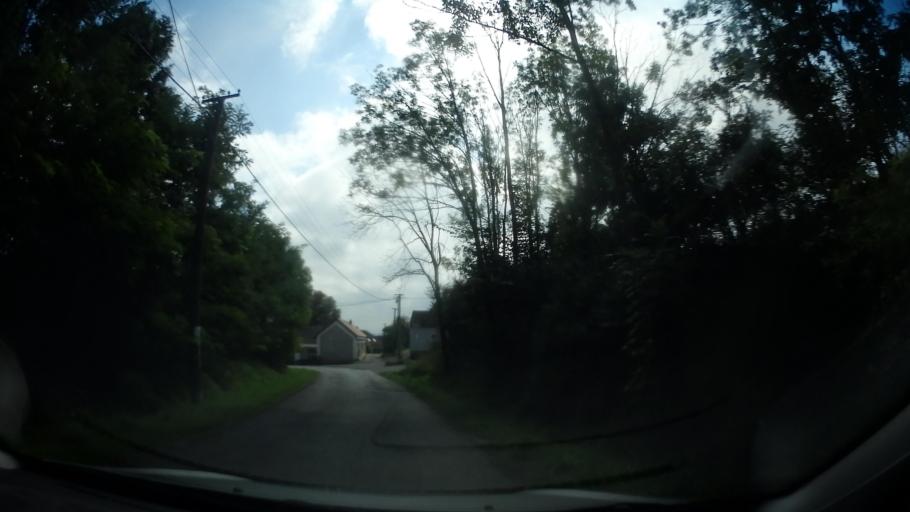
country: CZ
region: Central Bohemia
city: Sedlcany
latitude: 49.7119
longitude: 14.3691
